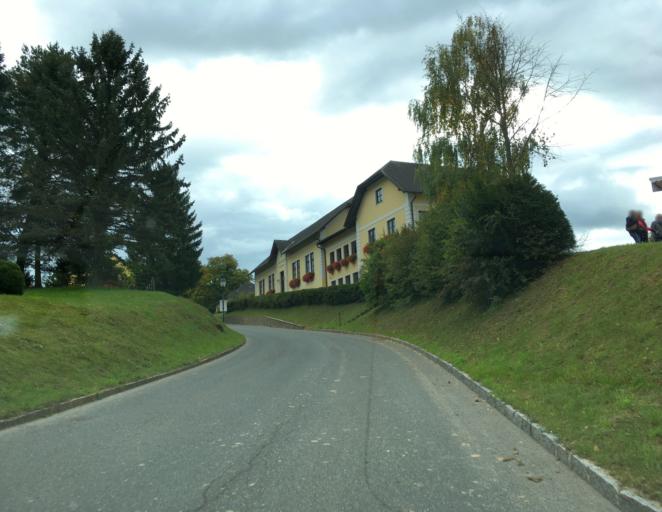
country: AT
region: Lower Austria
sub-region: Politischer Bezirk Wiener Neustadt
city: Bad Schonau
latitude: 47.4944
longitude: 16.2351
